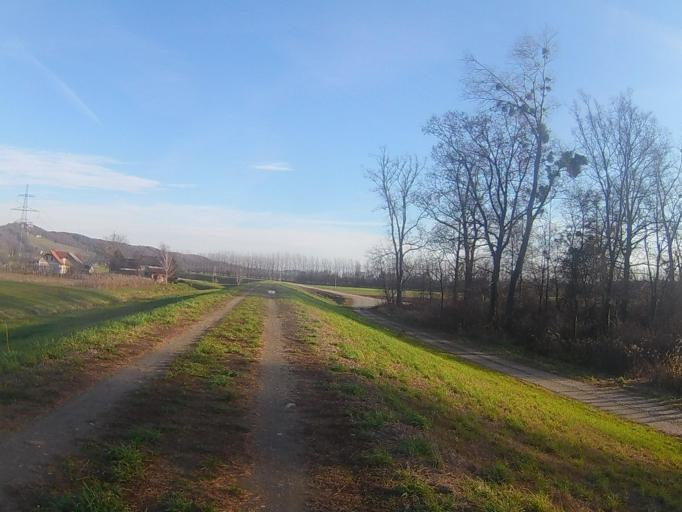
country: SI
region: Duplek
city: Spodnji Duplek
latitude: 46.4902
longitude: 15.7548
